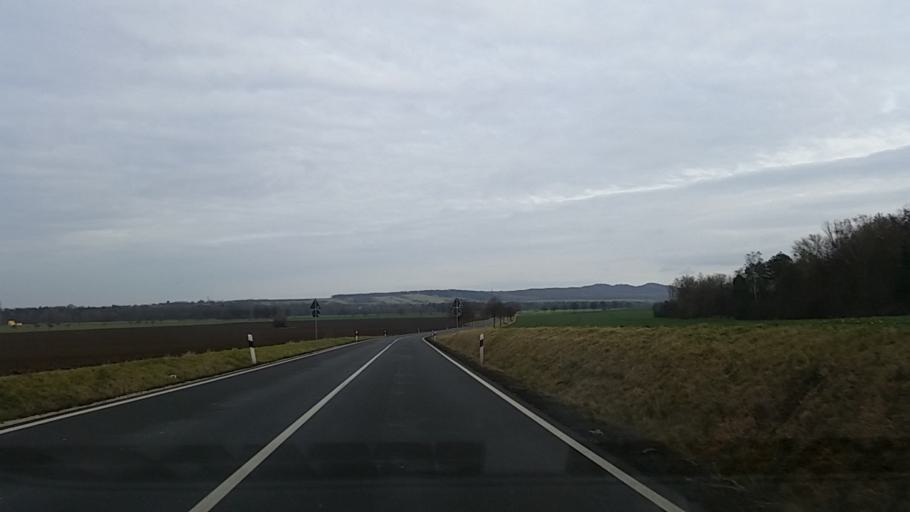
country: DE
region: Lower Saxony
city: Alt Wallmoden
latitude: 52.0180
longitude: 10.3182
